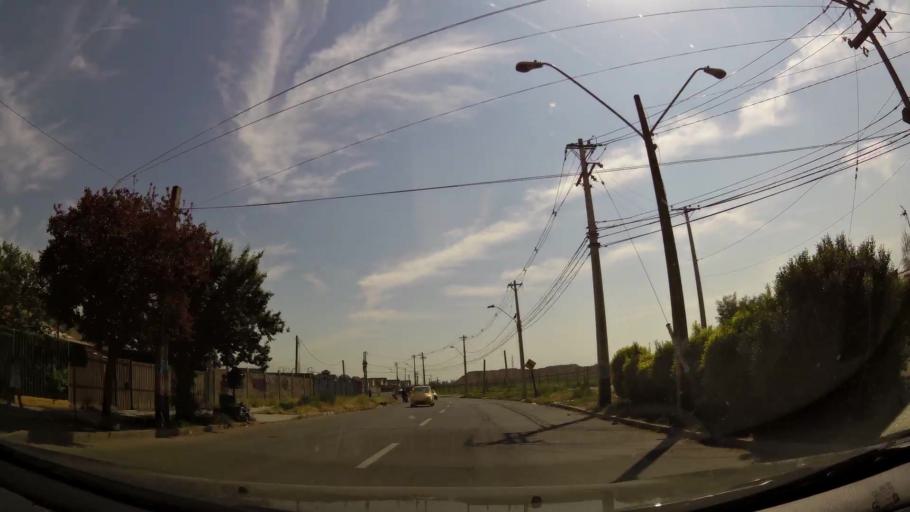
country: CL
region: Santiago Metropolitan
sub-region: Provincia de Cordillera
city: Puente Alto
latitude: -33.5774
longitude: -70.5925
